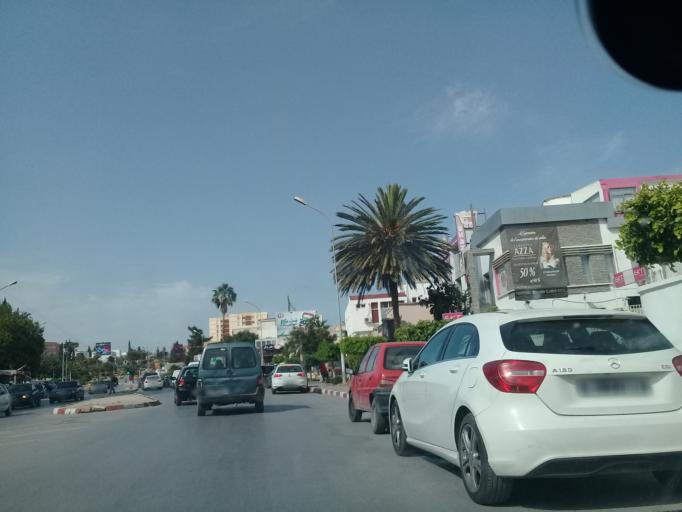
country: TN
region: Tunis
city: Tunis
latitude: 36.8446
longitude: 10.1664
